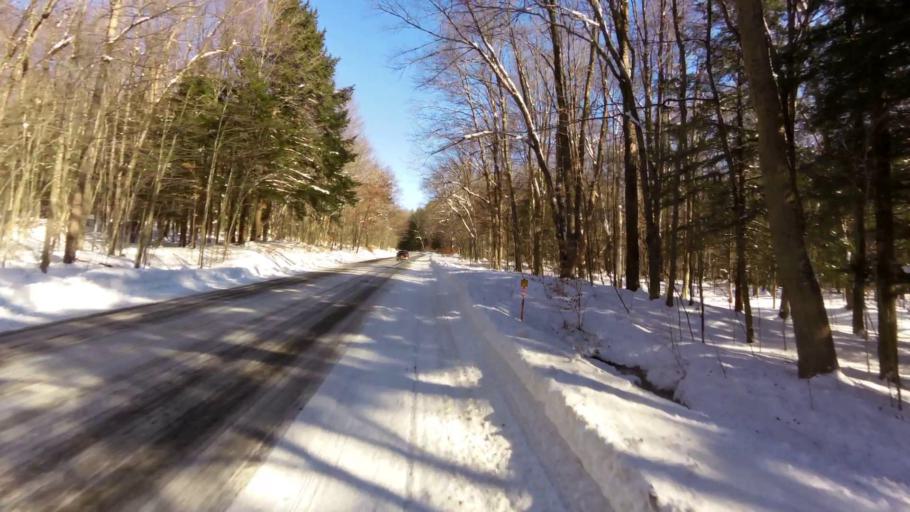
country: US
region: New York
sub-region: Cattaraugus County
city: Salamanca
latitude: 42.1204
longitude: -78.7312
